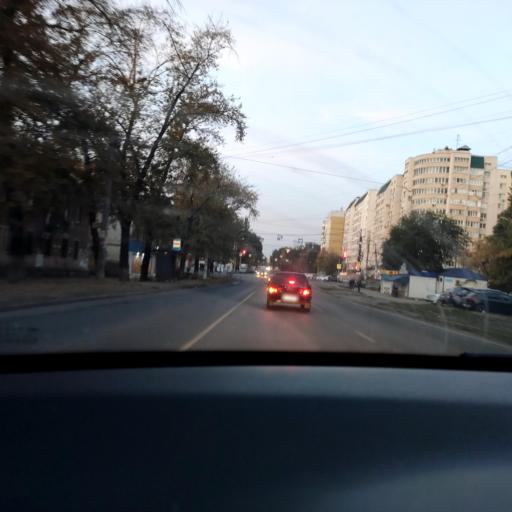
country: RU
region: Samara
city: Samara
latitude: 53.2304
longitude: 50.2508
